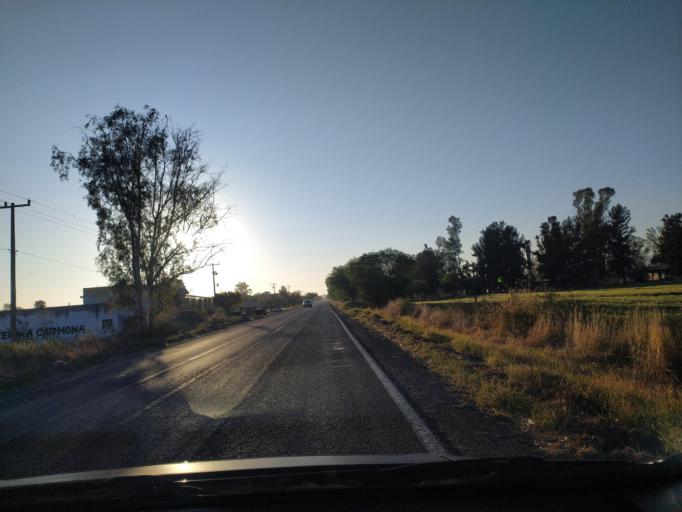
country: MX
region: Guanajuato
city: Ciudad Manuel Doblado
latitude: 20.7426
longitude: -101.8896
